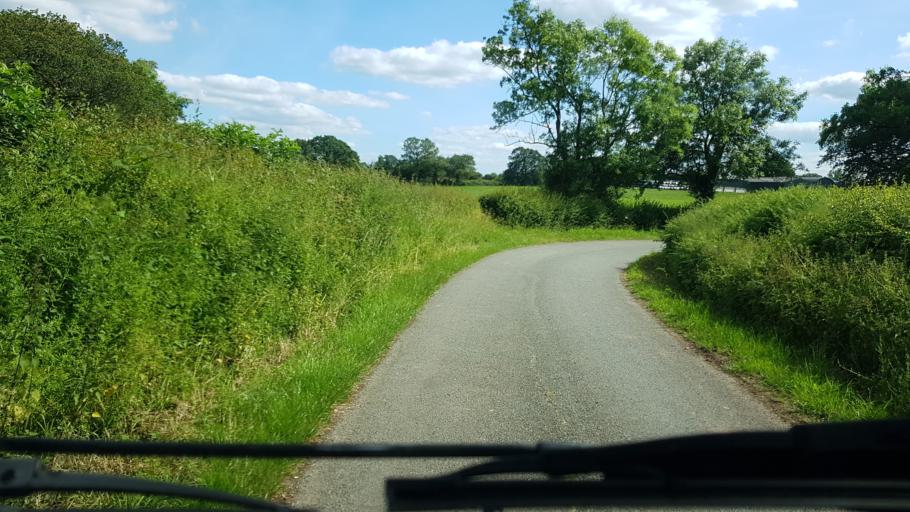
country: GB
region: England
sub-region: Shropshire
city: Romsley
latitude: 52.4552
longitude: -2.2914
